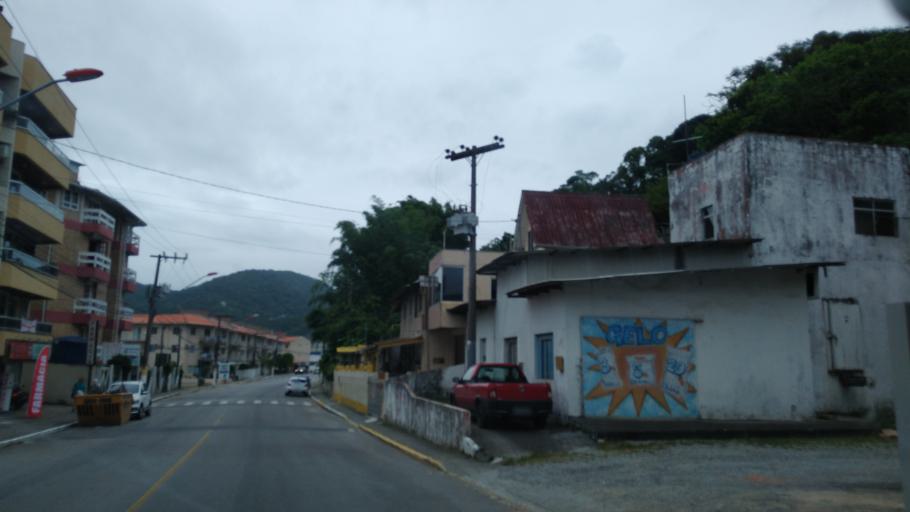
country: BR
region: Santa Catarina
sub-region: Itapema
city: Itapema
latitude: -27.0901
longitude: -48.6084
